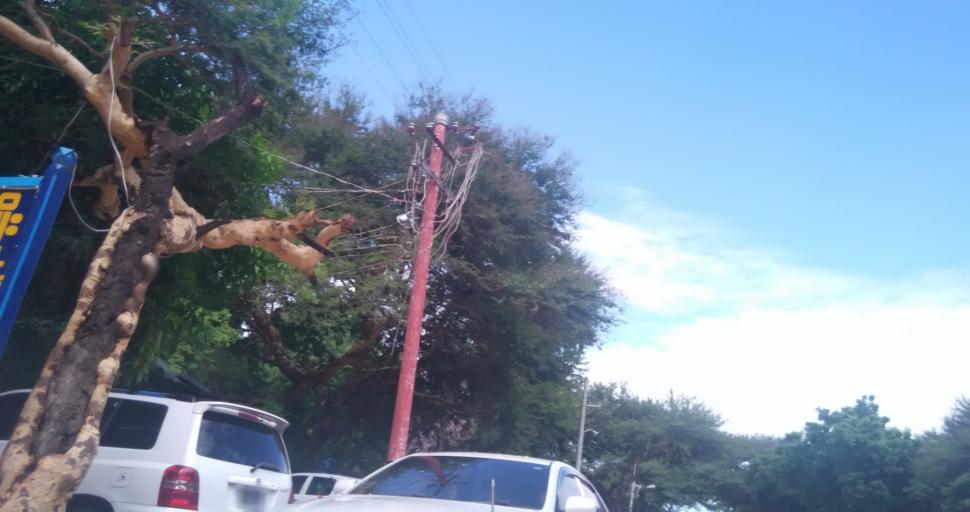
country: MM
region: Magway
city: Pakokku
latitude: 21.1885
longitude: 94.8911
